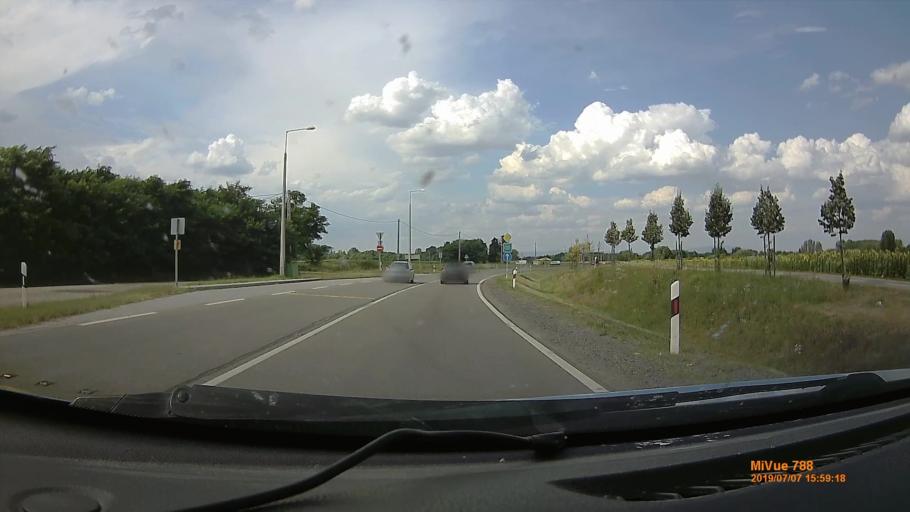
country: HU
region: Heves
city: Boldog
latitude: 47.5856
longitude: 19.7463
